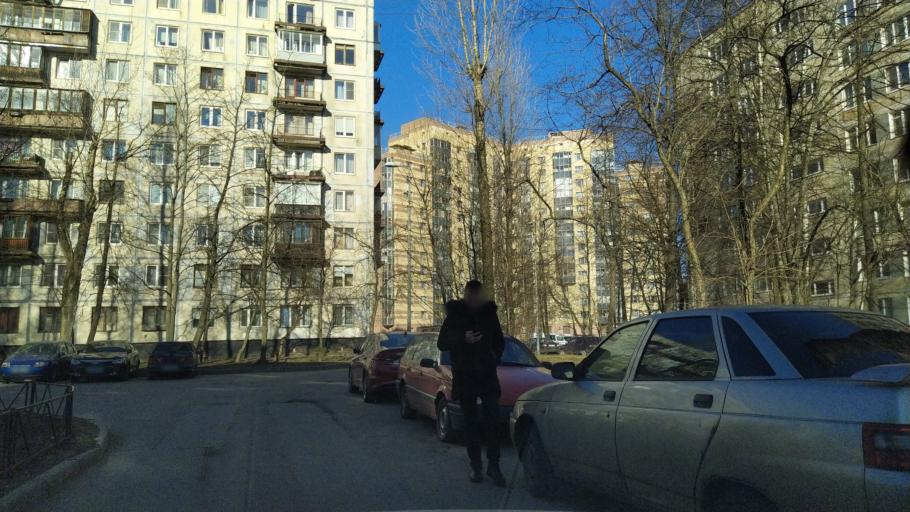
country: RU
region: Leningrad
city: Akademicheskoe
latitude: 60.0150
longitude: 30.4081
